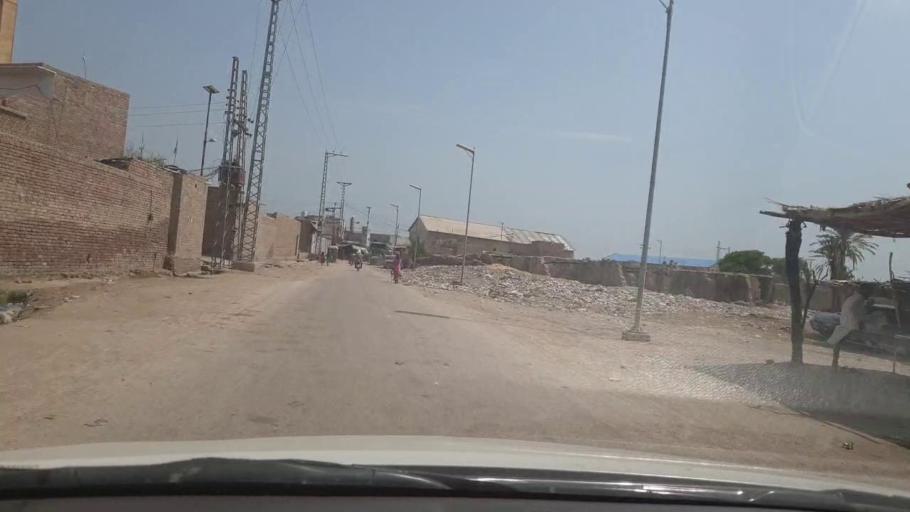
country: PK
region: Sindh
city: Garhi Yasin
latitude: 27.9045
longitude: 68.5071
